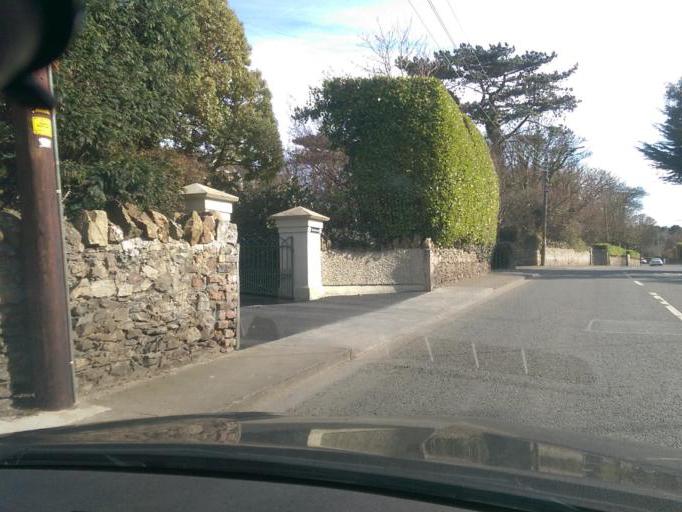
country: IE
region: Leinster
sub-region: Fingal County
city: Howth
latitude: 53.3800
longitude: -6.0574
